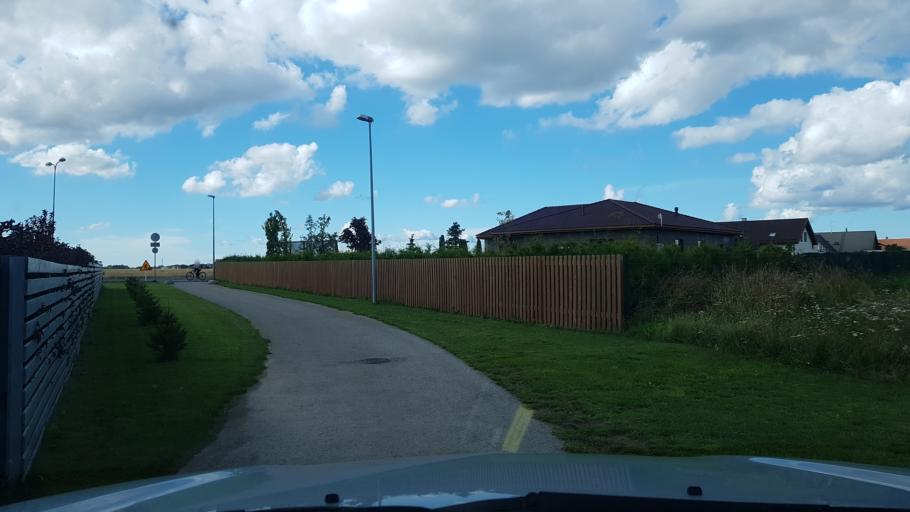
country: EE
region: Harju
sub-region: Rae vald
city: Jueri
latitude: 59.3750
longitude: 24.8333
